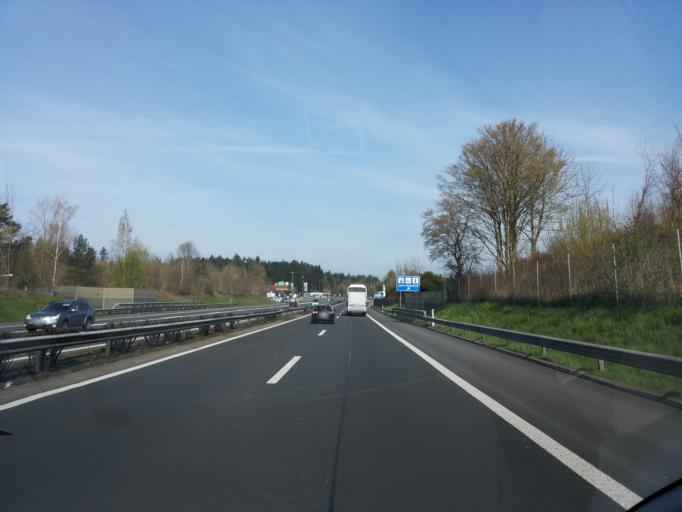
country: CH
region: Lucerne
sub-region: Sursee District
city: Neuenkirch
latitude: 47.1093
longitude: 8.2372
